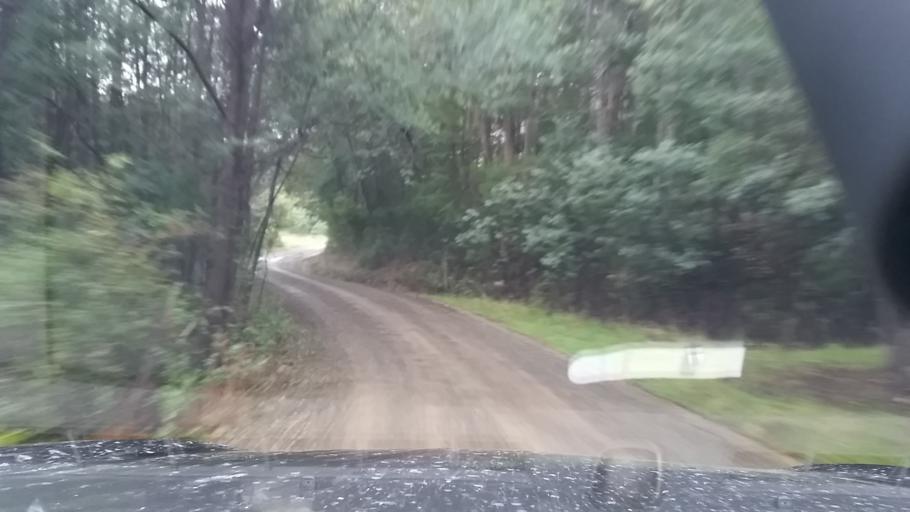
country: NZ
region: Nelson
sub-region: Nelson City
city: Nelson
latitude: -41.3747
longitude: 173.5970
